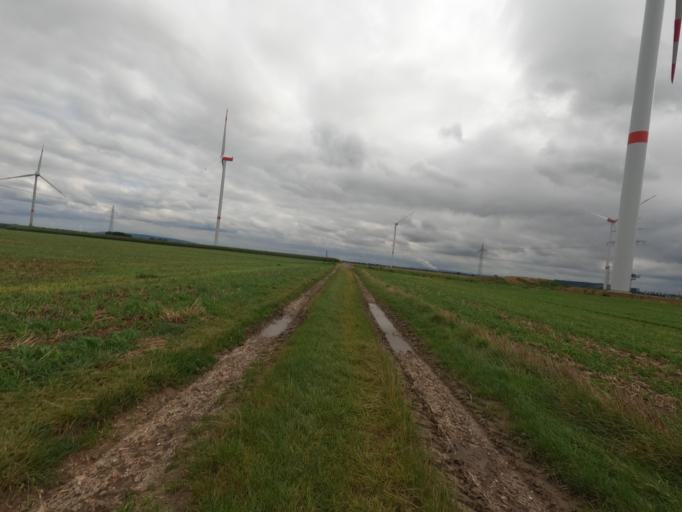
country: DE
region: North Rhine-Westphalia
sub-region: Regierungsbezirk Koln
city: Linnich
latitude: 50.9787
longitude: 6.2248
